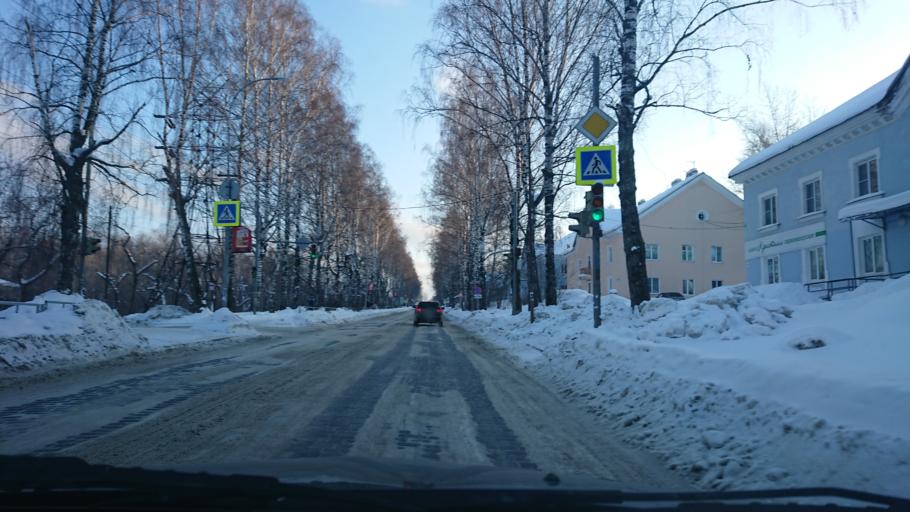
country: RU
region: Sverdlovsk
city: Degtyarsk
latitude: 56.6970
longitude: 60.0879
